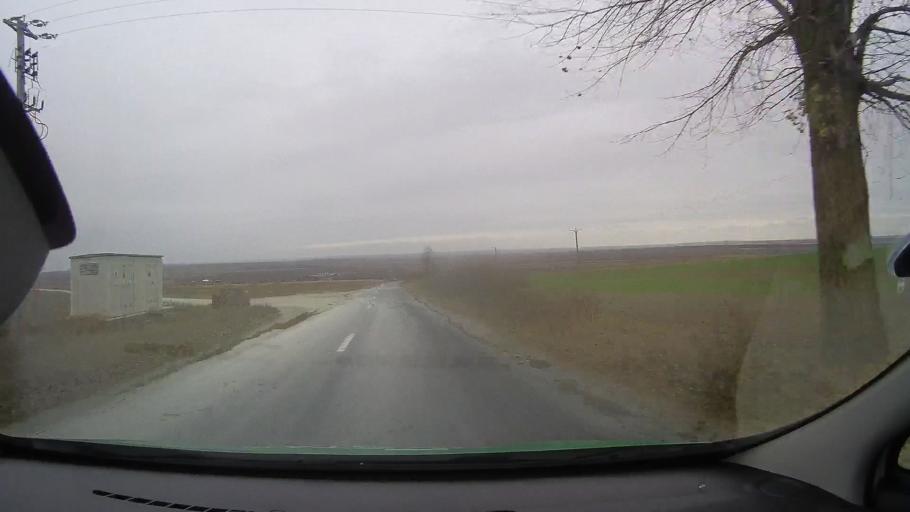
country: RO
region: Constanta
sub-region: Comuna Pantelimon
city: Pantelimon
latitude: 44.5880
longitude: 28.3163
